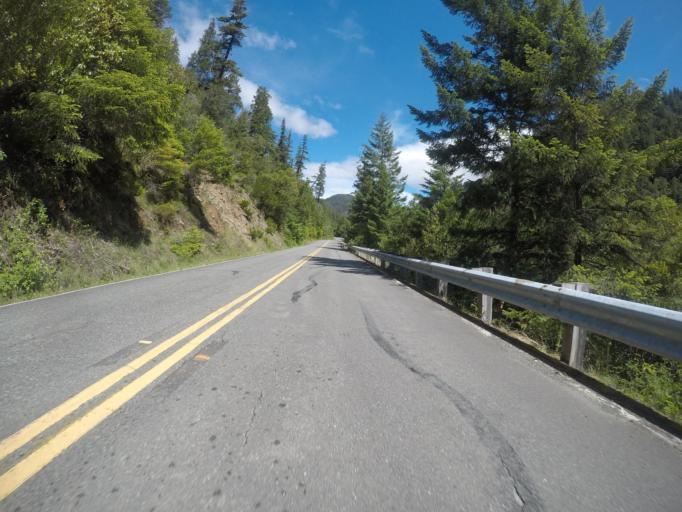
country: US
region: California
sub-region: Del Norte County
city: Bertsch-Oceanview
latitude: 41.7084
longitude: -123.9413
